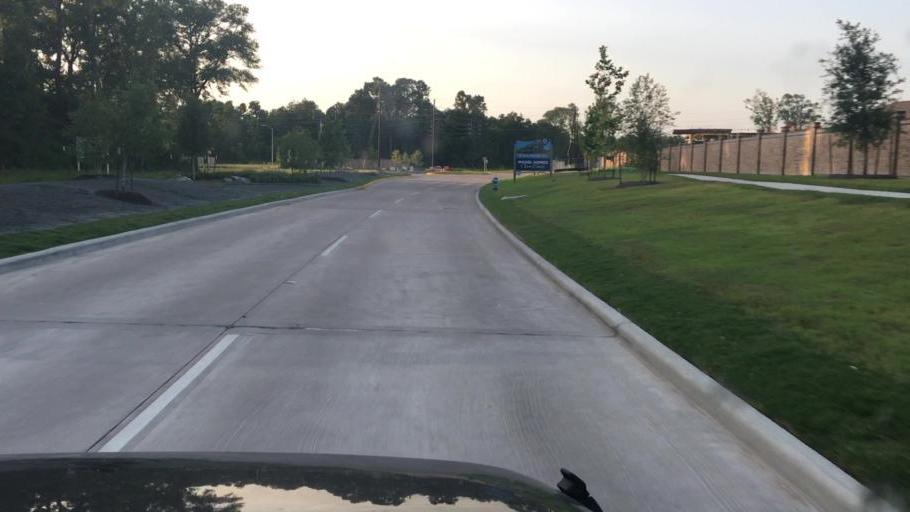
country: US
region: Texas
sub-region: Harris County
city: Atascocita
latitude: 29.9450
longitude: -95.2113
